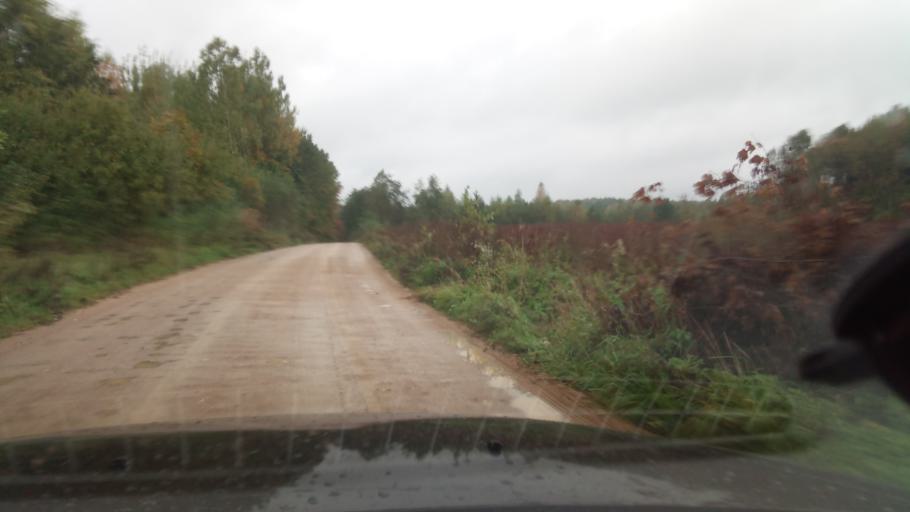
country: LT
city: Skaidiskes
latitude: 54.5577
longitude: 25.4922
